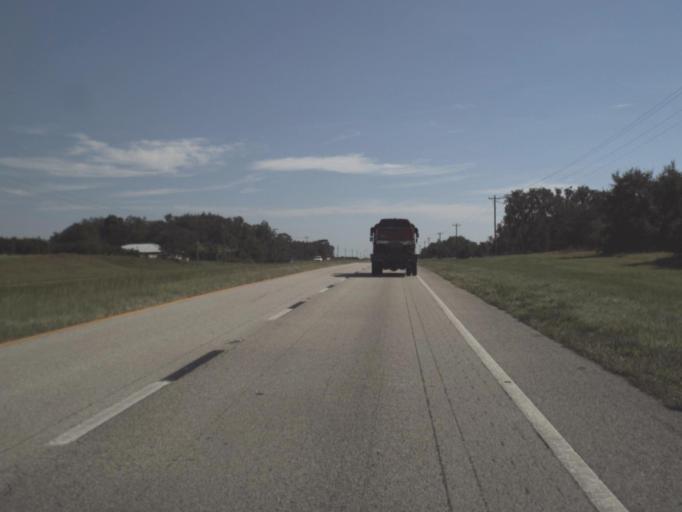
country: US
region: Florida
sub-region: Highlands County
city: Lake Placid
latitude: 27.3890
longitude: -81.4127
